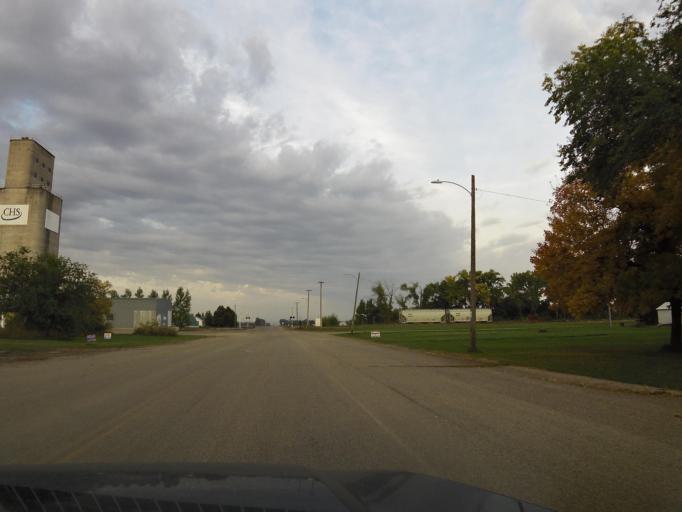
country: US
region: North Dakota
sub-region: Pembina County
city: Cavalier
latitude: 48.6882
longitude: -97.6672
